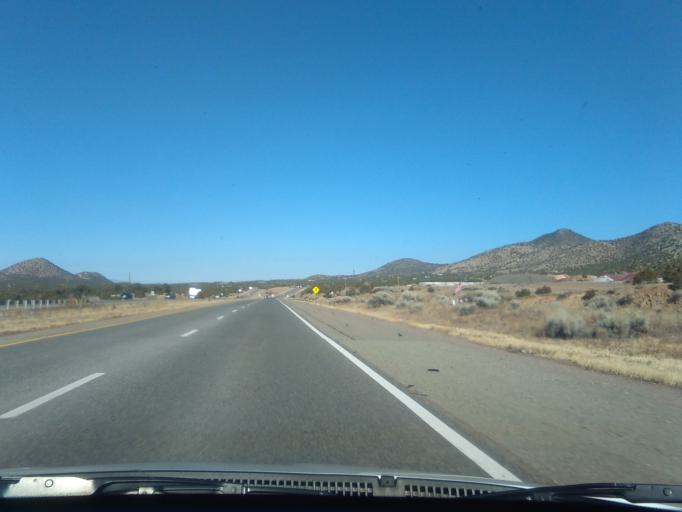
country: US
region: New Mexico
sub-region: Santa Fe County
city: Eldorado at Santa Fe
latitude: 35.5555
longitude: -105.8791
